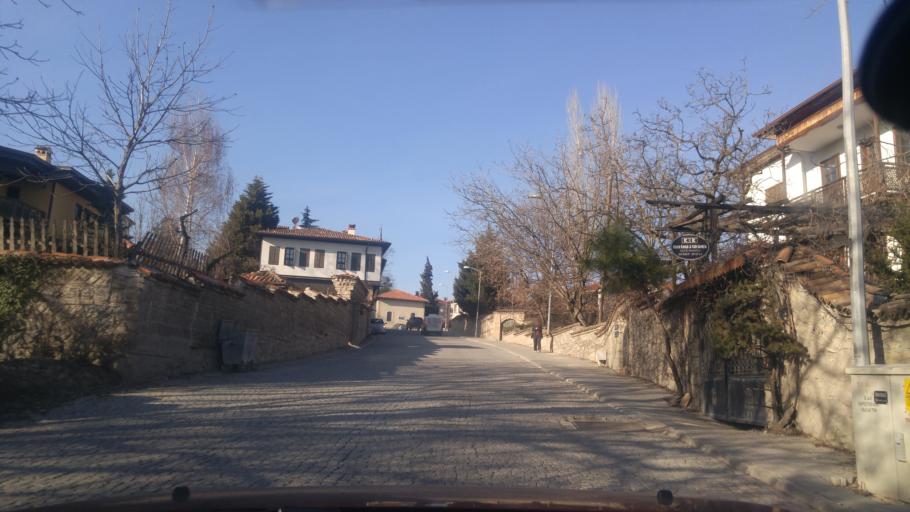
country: TR
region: Karabuk
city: Safranbolu
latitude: 41.2613
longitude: 32.6746
